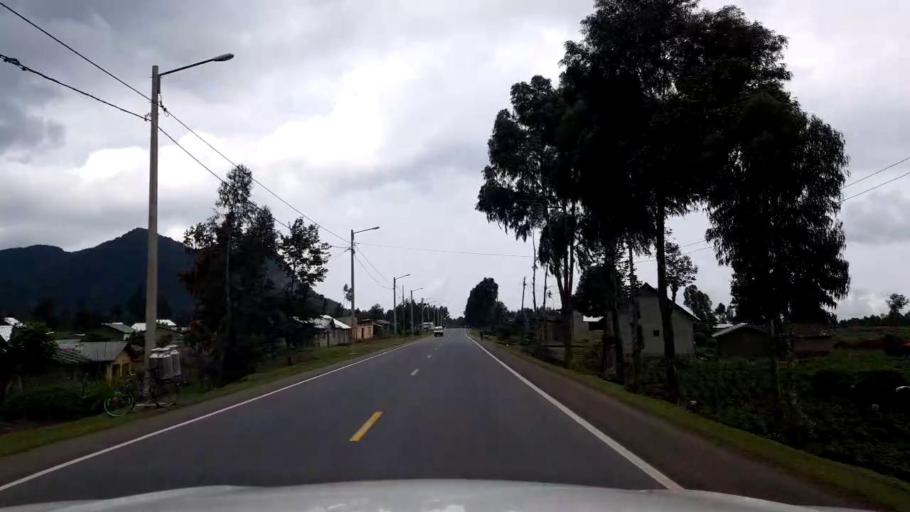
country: RW
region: Western Province
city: Gisenyi
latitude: -1.6353
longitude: 29.4085
